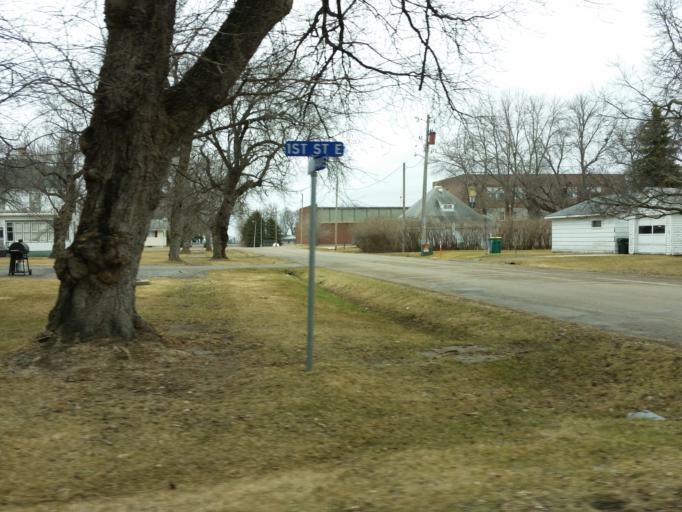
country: US
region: North Dakota
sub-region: Traill County
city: Hillsboro
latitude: 47.1917
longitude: -97.2161
